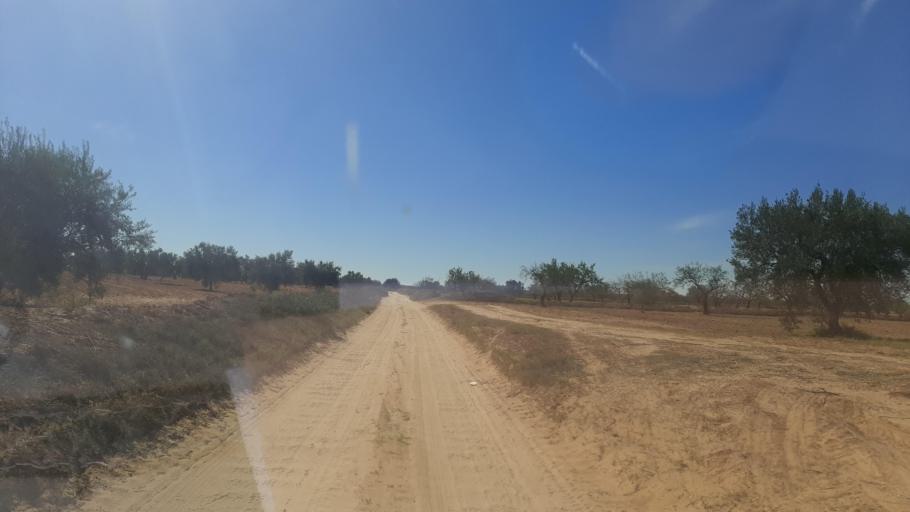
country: TN
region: Safaqis
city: Sfax
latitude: 34.8235
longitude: 10.5530
